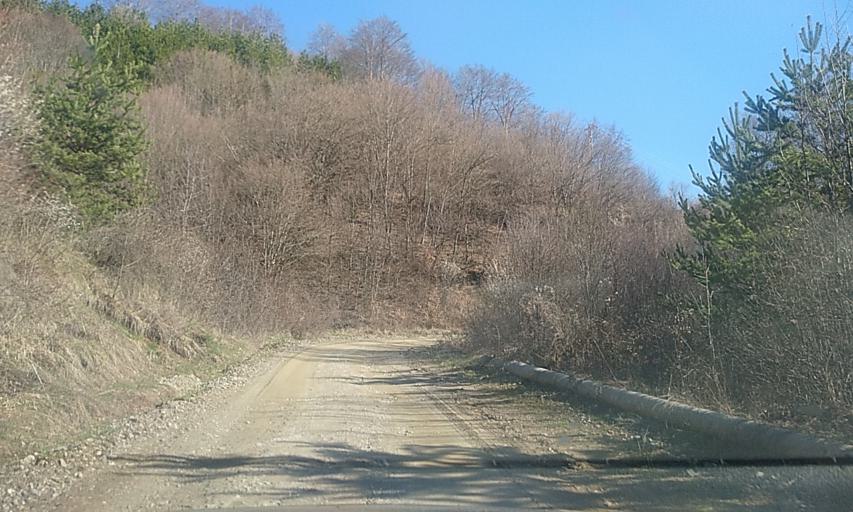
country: MK
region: Kriva Palanka
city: Kriva Palanka
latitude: 42.3421
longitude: 22.3612
